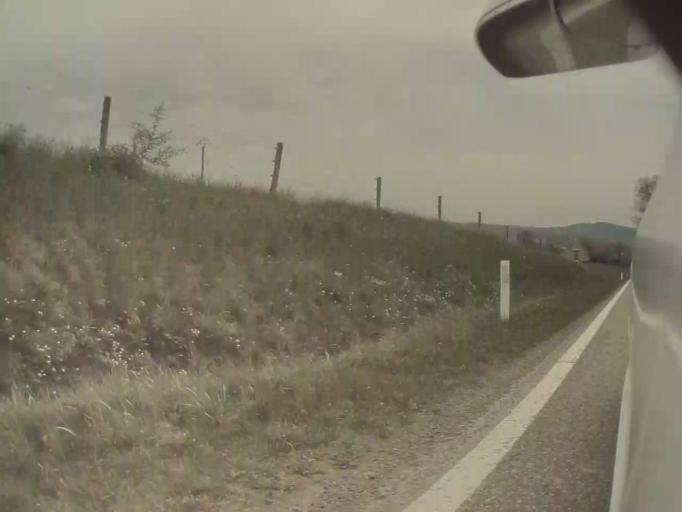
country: BE
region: Wallonia
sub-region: Province du Luxembourg
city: Manhay
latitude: 50.3765
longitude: 5.7112
